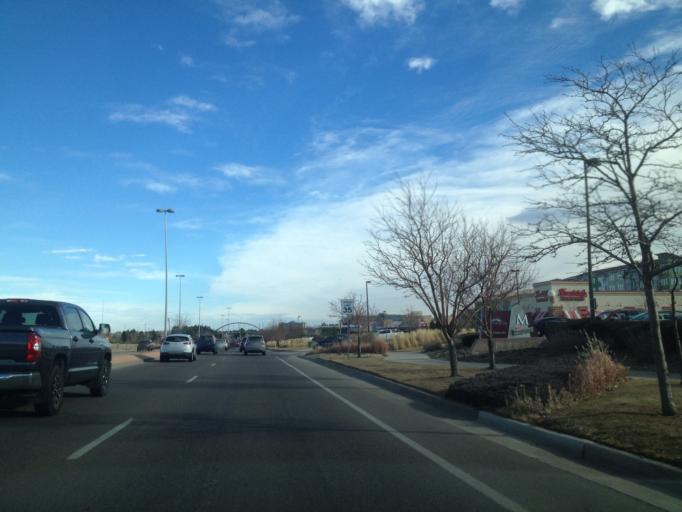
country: US
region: Colorado
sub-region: Boulder County
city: Superior
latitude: 39.9287
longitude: -105.1419
